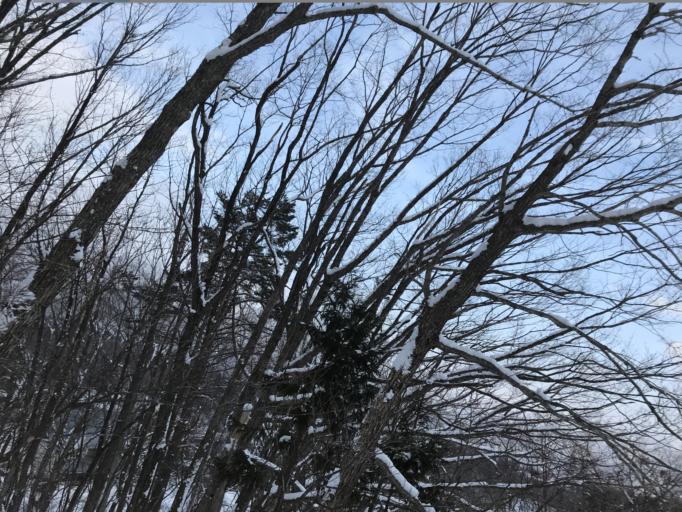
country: JP
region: Nagano
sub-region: Kitaazumi Gun
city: Hakuba
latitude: 36.7045
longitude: 137.8335
